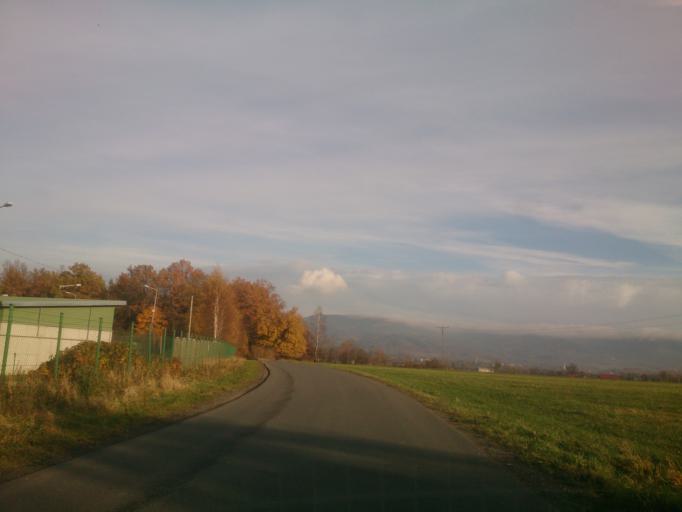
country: PL
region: Lower Silesian Voivodeship
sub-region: Powiat jeleniogorski
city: Myslakowice
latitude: 50.8024
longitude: 15.7874
